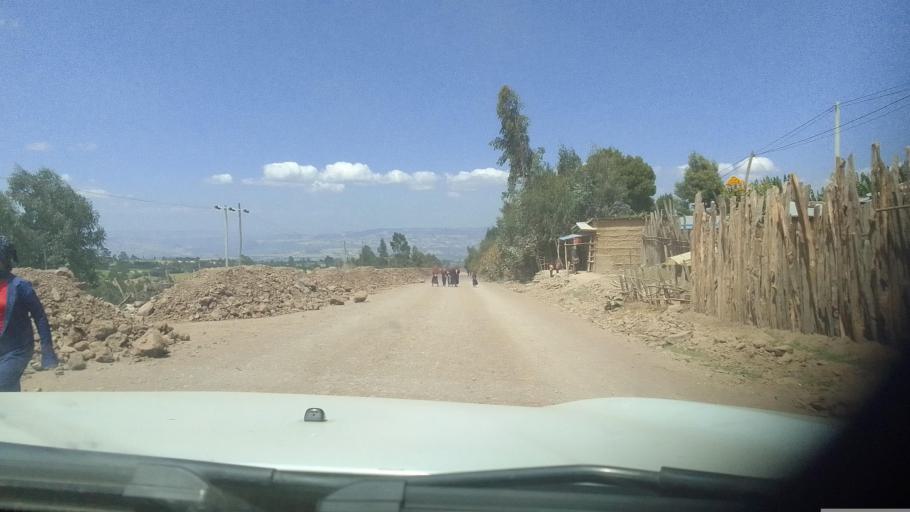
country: ET
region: Oromiya
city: Hagere Hiywet
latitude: 8.8561
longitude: 37.8924
